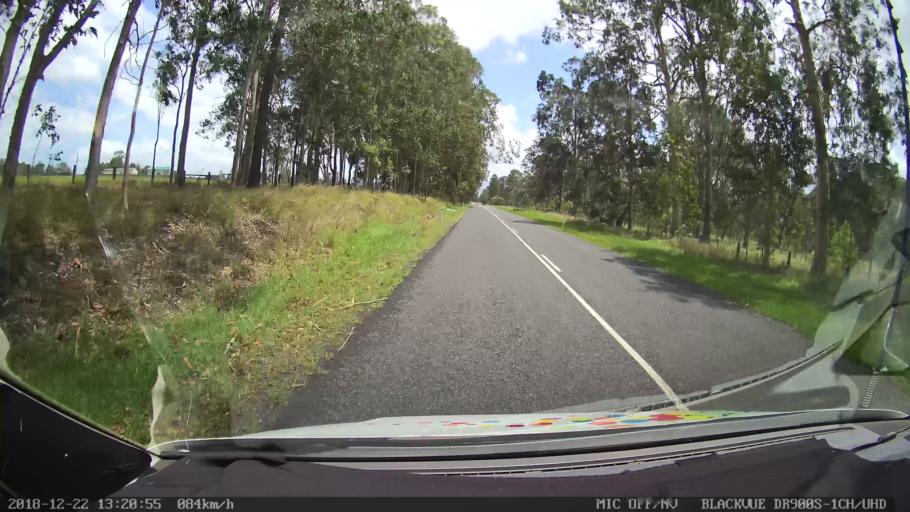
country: AU
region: New South Wales
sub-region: Clarence Valley
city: Coutts Crossing
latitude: -29.7718
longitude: 152.9250
